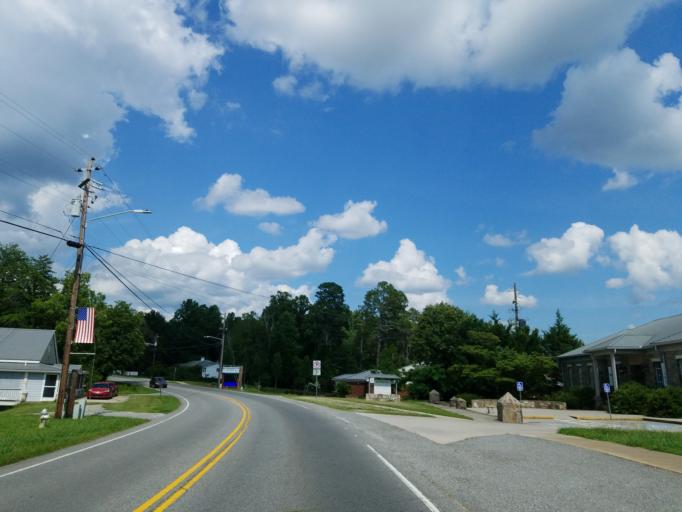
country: US
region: Georgia
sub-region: Dawson County
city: Dawsonville
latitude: 34.4212
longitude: -84.1129
